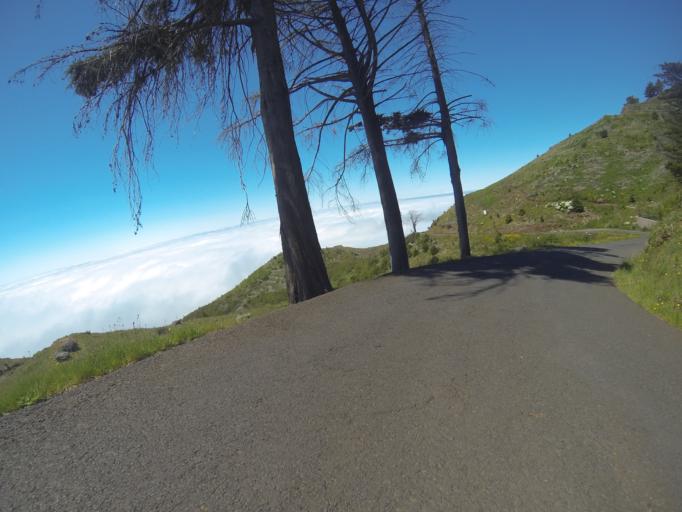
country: PT
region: Madeira
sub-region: Funchal
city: Nossa Senhora do Monte
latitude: 32.7044
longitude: -16.9115
